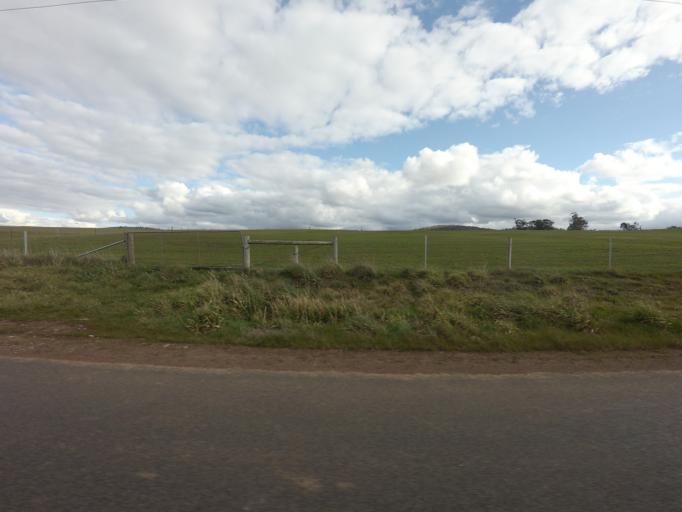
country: AU
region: Tasmania
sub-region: Northern Midlands
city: Evandale
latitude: -41.8895
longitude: 147.3267
